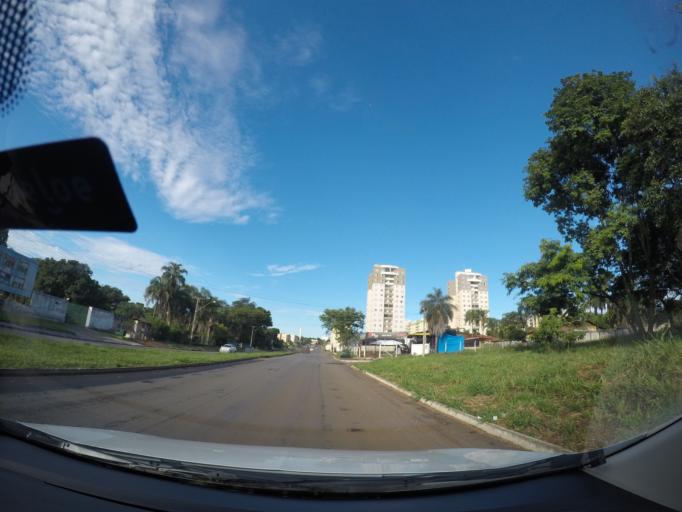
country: BR
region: Goias
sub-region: Goiania
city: Goiania
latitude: -16.7472
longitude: -49.2708
